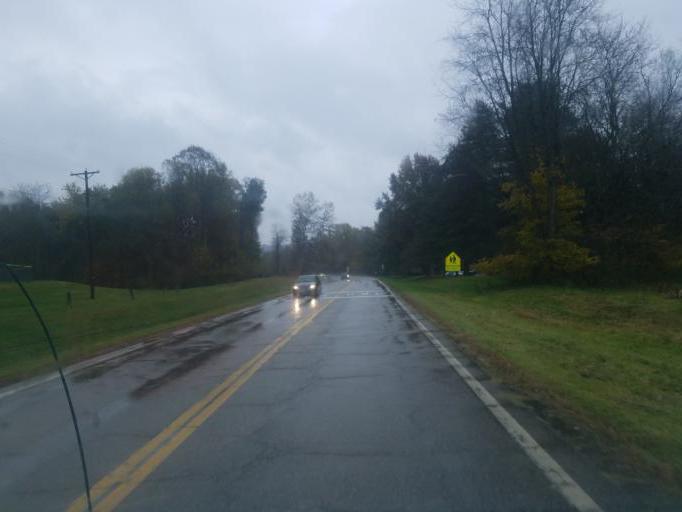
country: US
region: Ohio
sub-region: Morgan County
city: McConnelsville
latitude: 39.6137
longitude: -81.8256
